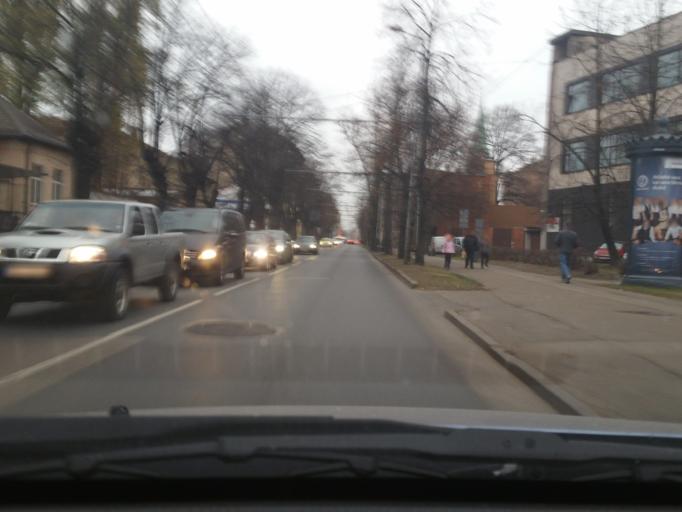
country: LV
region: Riga
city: Riga
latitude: 56.9653
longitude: 24.1335
